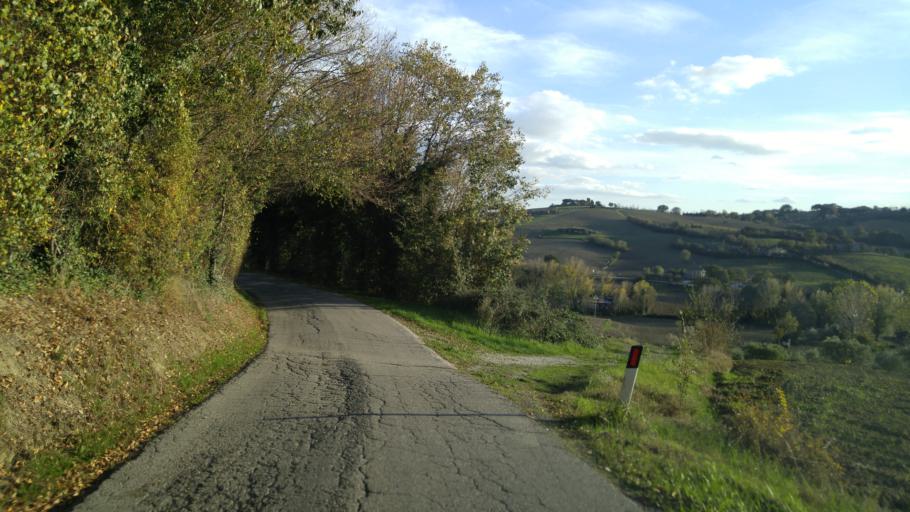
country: IT
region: The Marches
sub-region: Provincia di Pesaro e Urbino
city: Calcinelli
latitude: 43.7801
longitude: 12.9115
